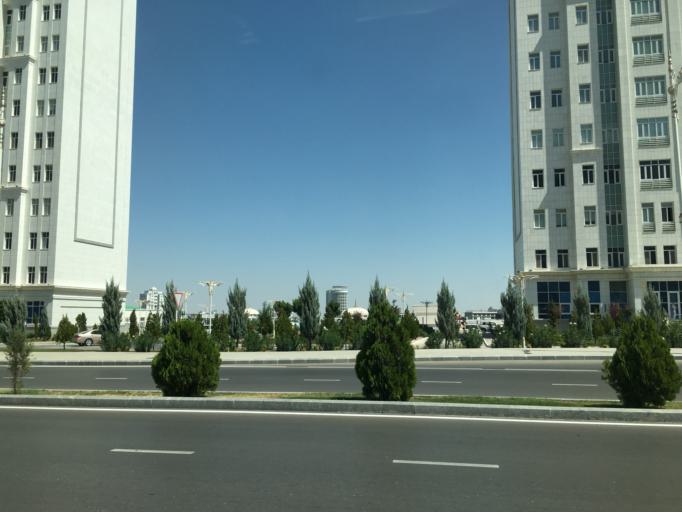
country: TM
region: Ahal
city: Ashgabat
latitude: 37.9315
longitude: 58.3683
